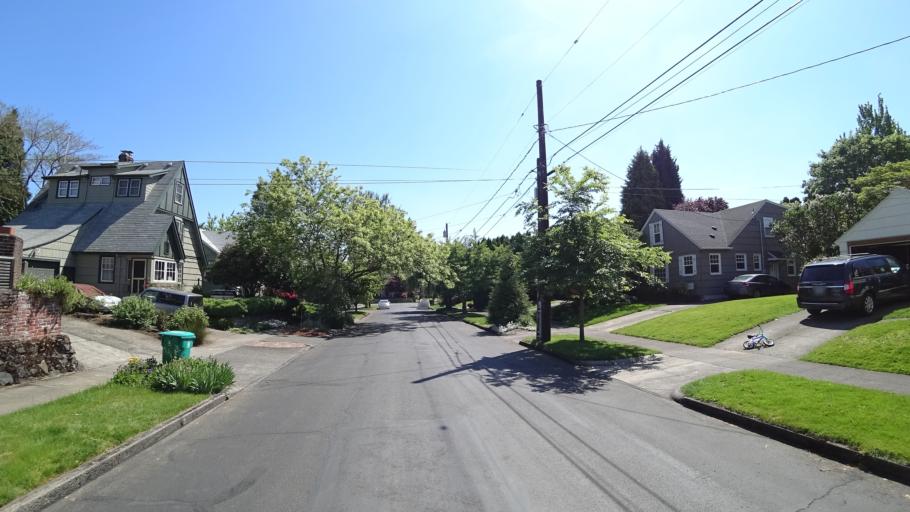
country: US
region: Oregon
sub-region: Multnomah County
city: Portland
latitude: 45.5098
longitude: -122.6358
